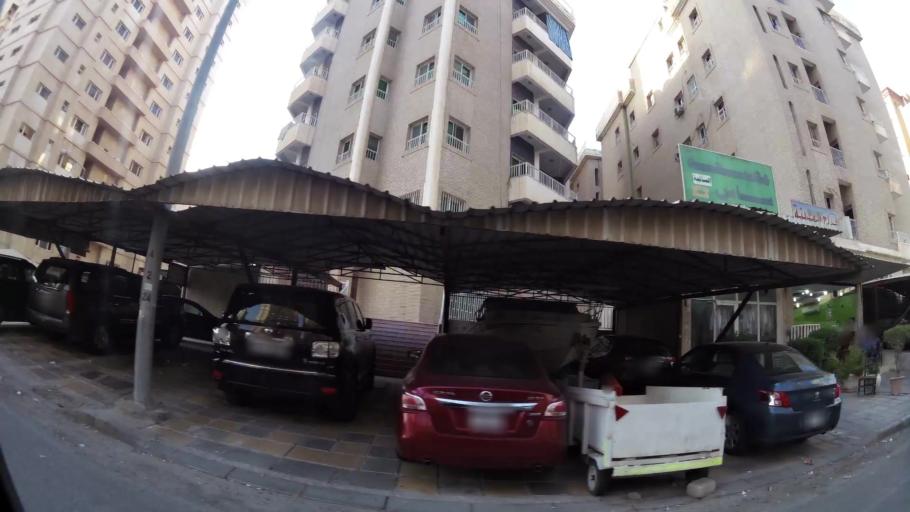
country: KW
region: Muhafazat Hawalli
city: As Salimiyah
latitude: 29.3333
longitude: 48.0783
